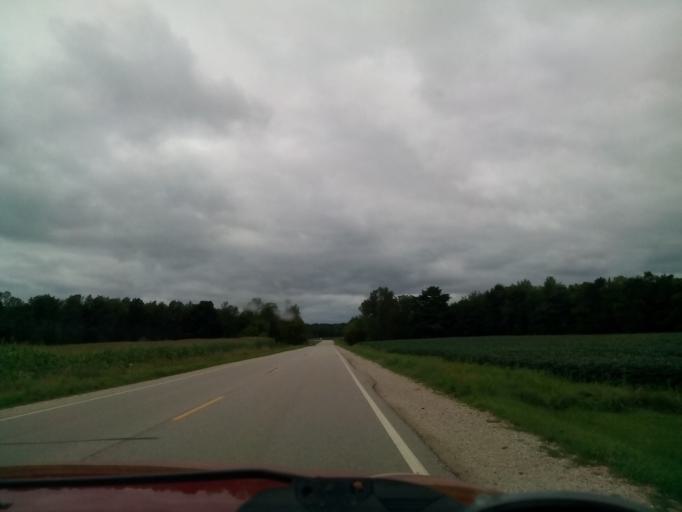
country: US
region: Wisconsin
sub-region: Menominee County
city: Legend Lake
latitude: 44.9990
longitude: -88.4282
